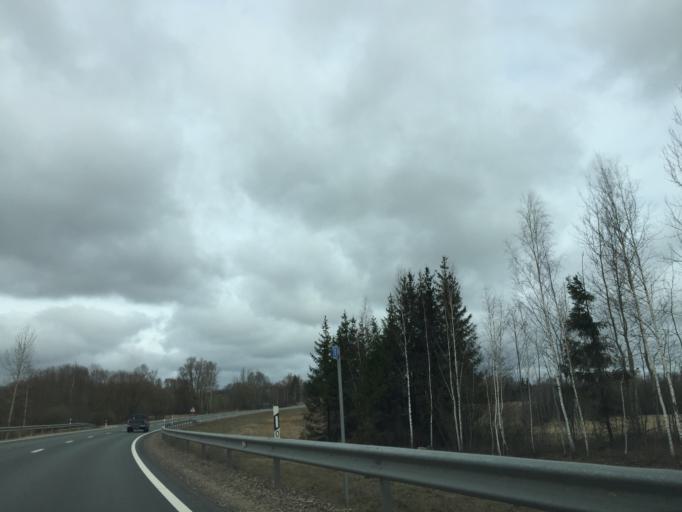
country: LV
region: Daugavpils
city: Daugavpils
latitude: 55.8694
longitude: 26.4187
